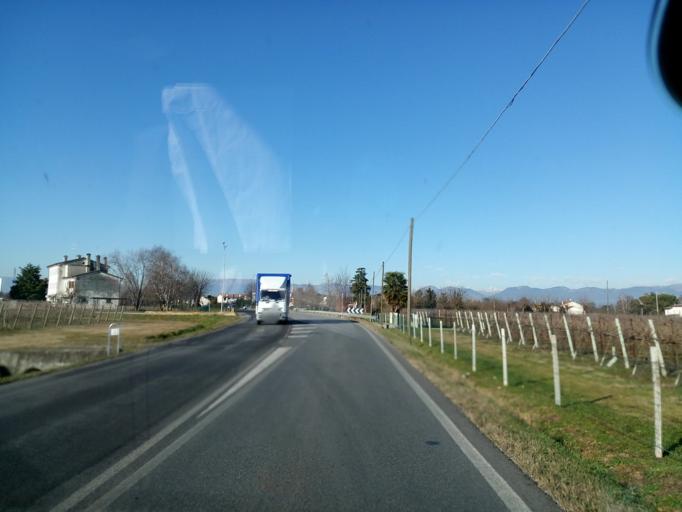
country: IT
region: Veneto
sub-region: Provincia di Treviso
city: San Michele di Piave
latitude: 45.8087
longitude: 12.3611
